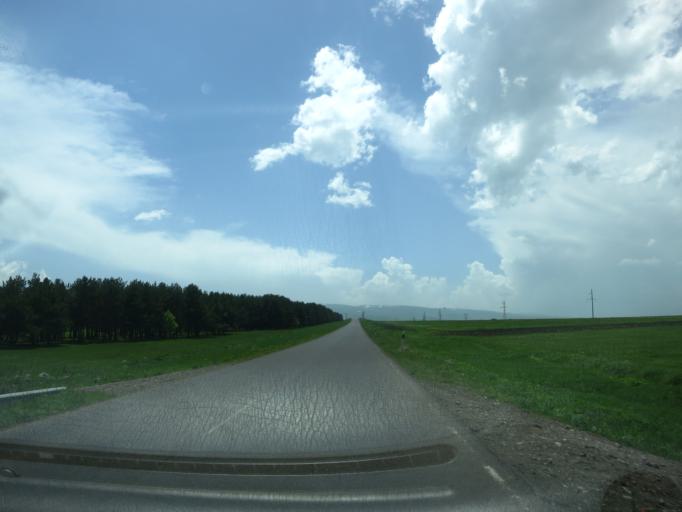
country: GE
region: Samtskhe-Javakheti
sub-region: Ninotsminda
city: Ninotsminda
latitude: 41.2776
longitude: 43.6164
